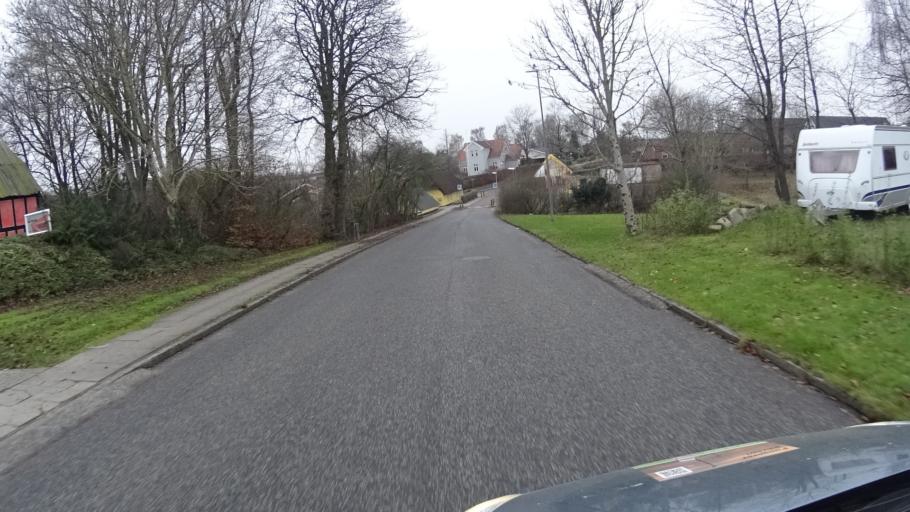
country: DK
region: South Denmark
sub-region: Vejle Kommune
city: Vejle
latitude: 55.7179
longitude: 9.6119
